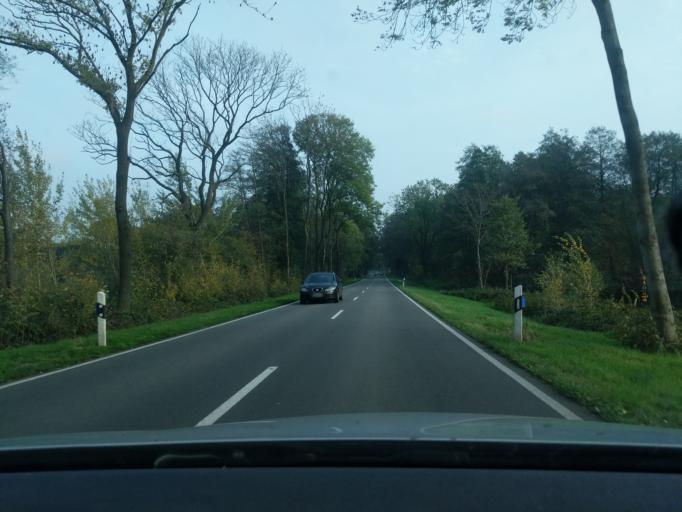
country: DE
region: Lower Saxony
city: Lamstedt
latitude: 53.6354
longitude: 9.1145
